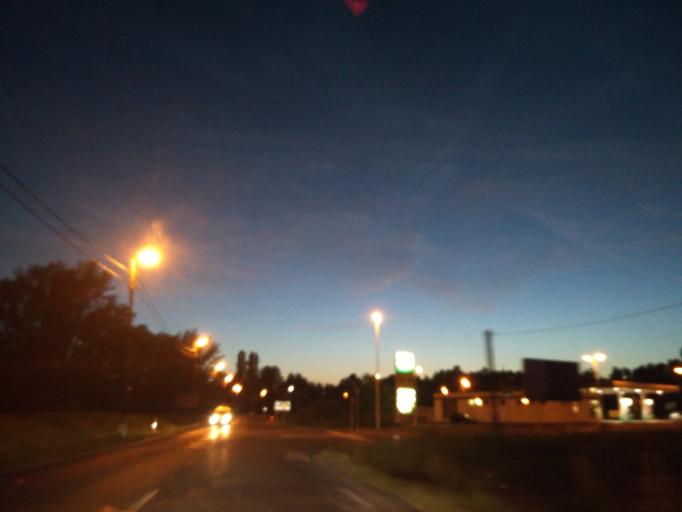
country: HU
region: Vas
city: Vasvar
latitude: 47.0539
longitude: 16.7913
